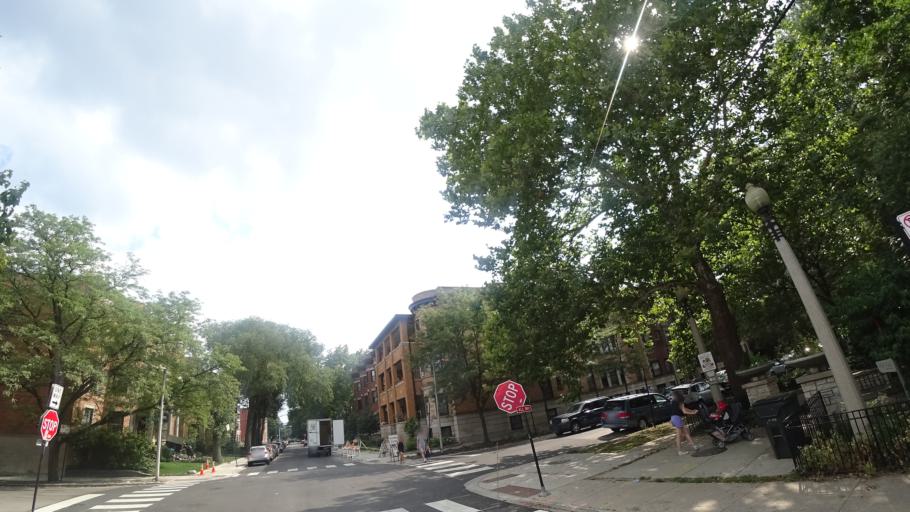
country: US
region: Illinois
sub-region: Cook County
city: Chicago
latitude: 41.8044
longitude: -87.5919
